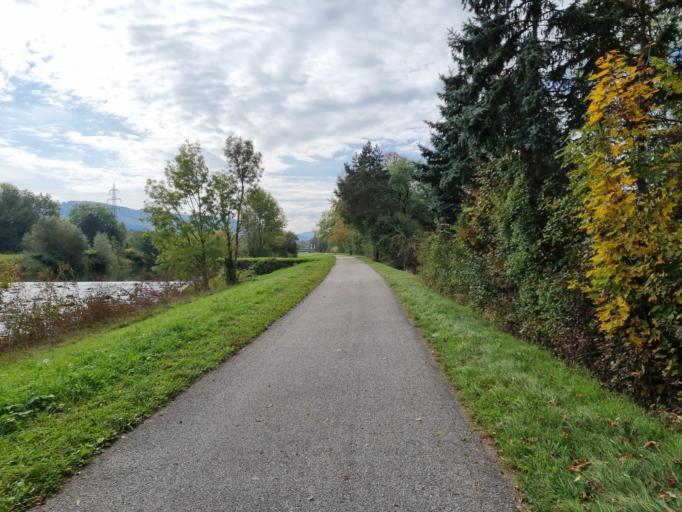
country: AT
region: Lower Austria
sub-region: Politischer Bezirk Sankt Polten
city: Wilhelmsburg
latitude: 48.1359
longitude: 15.6326
